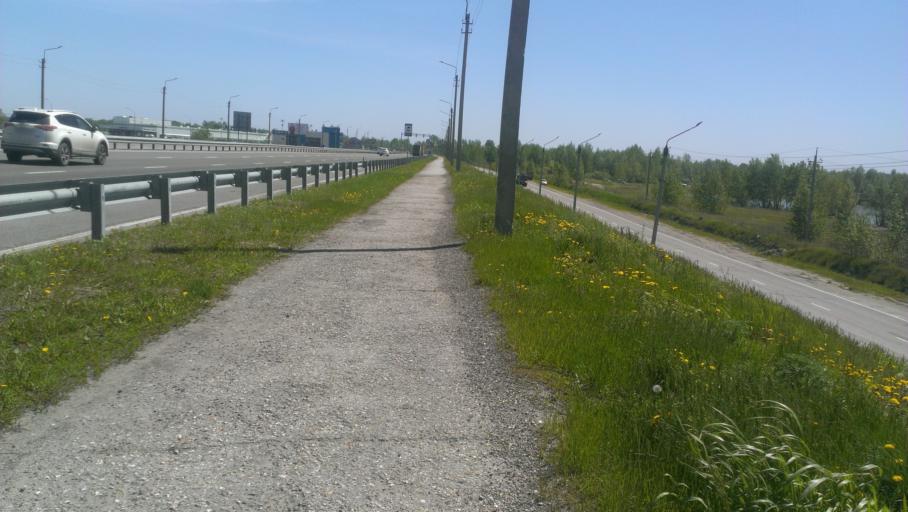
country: RU
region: Altai Krai
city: Zaton
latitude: 53.3183
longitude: 83.8181
